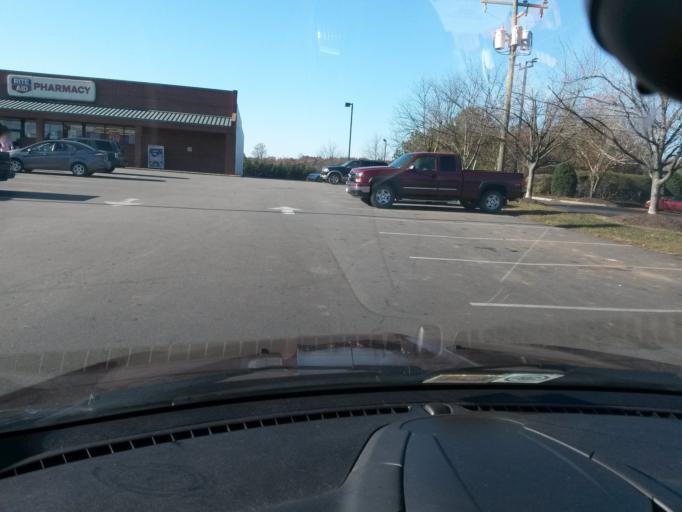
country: US
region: Virginia
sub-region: Charlotte County
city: Charlotte Court House
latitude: 37.0364
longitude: -78.4764
